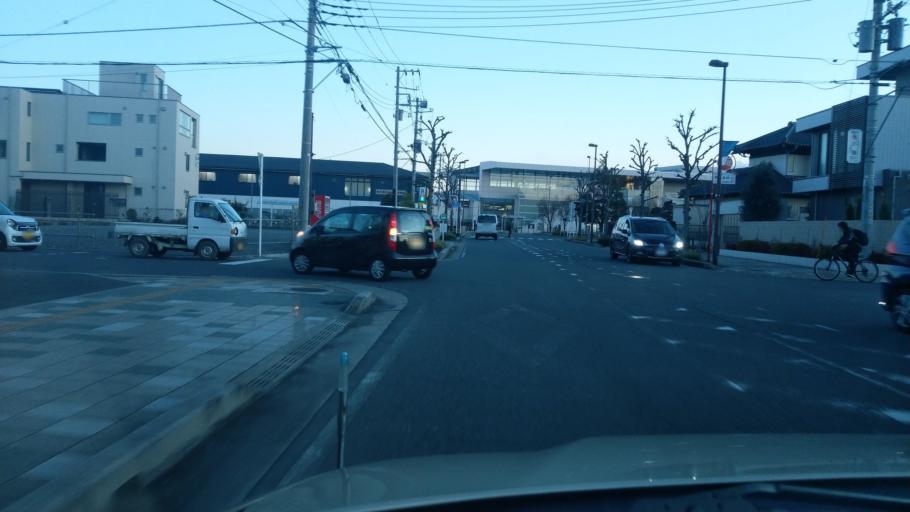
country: JP
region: Saitama
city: Ageoshimo
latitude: 35.9238
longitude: 139.5802
